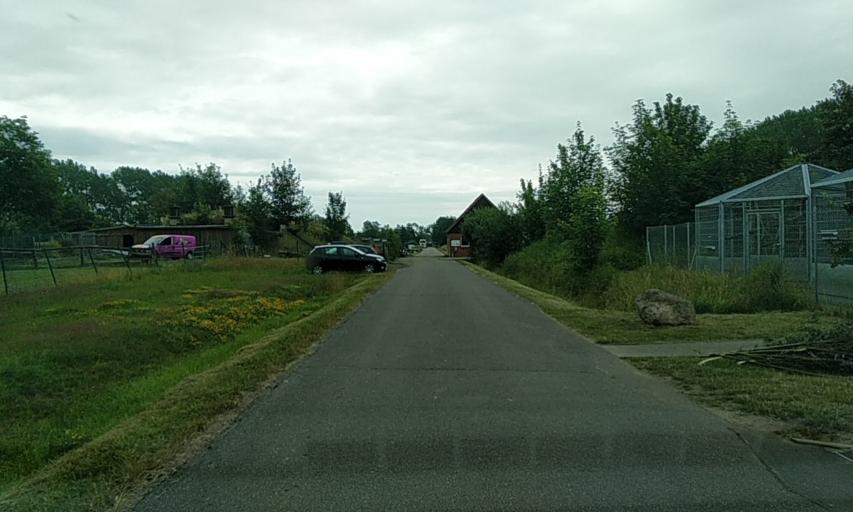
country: DE
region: Schleswig-Holstein
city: Brodersby
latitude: 54.6459
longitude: 10.0090
